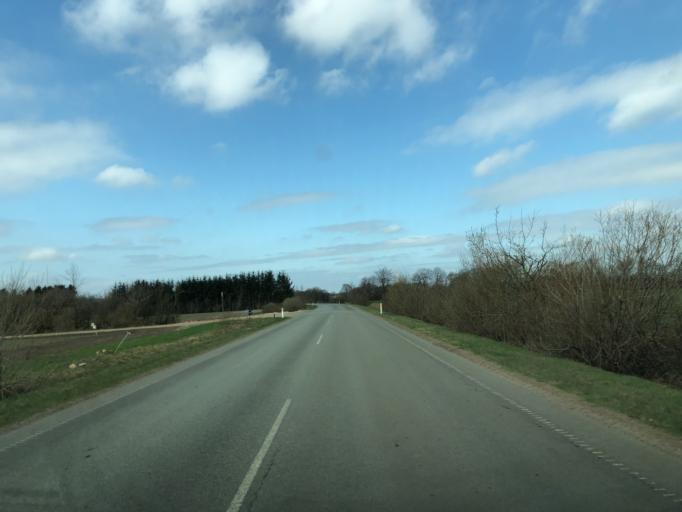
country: DK
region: Central Jutland
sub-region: Ikast-Brande Kommune
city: Brande
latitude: 55.9281
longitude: 9.1797
